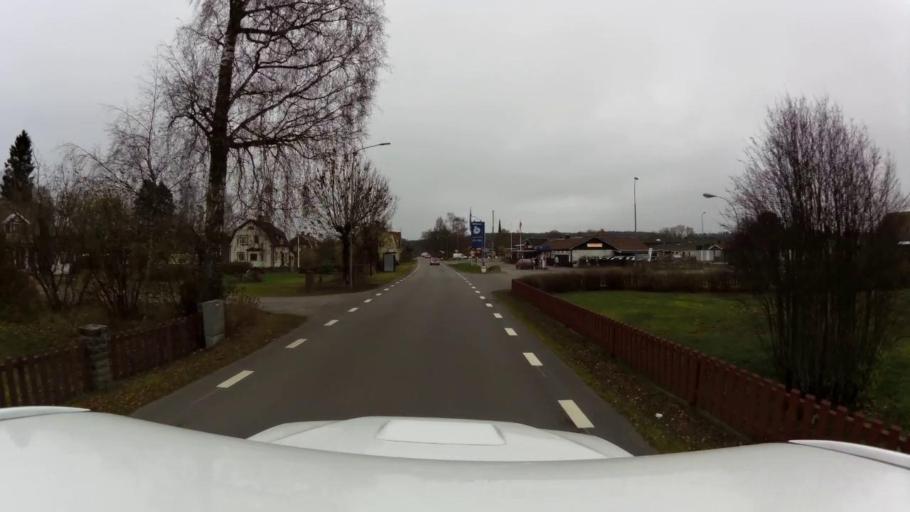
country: SE
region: OEstergoetland
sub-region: Kinda Kommun
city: Kisa
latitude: 58.1263
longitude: 15.4334
